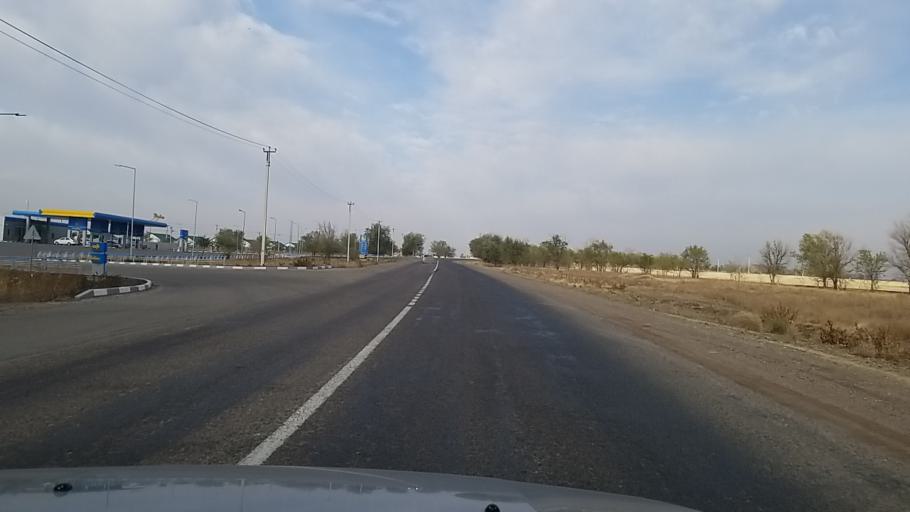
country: KZ
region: Almaty Oblysy
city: Burunday
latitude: 43.4772
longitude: 76.6846
